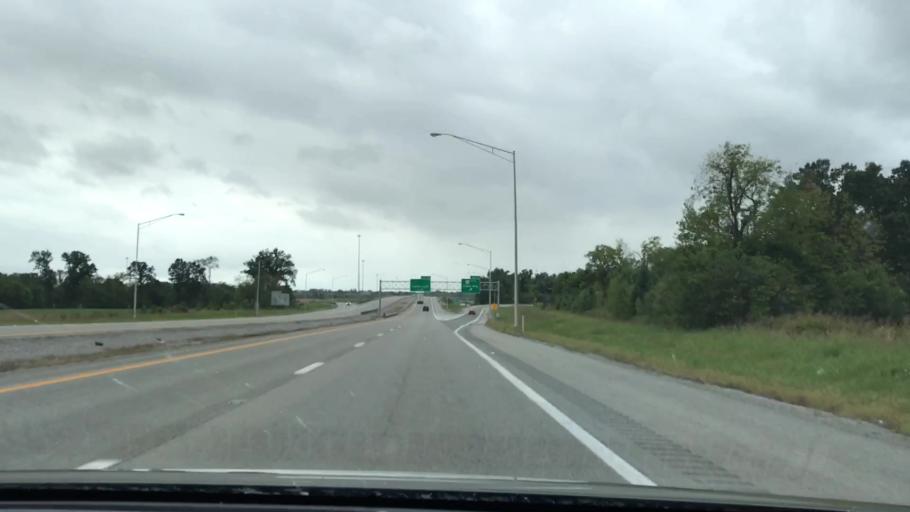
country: US
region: Kentucky
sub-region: Christian County
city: Hopkinsville
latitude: 36.8240
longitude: -87.4795
